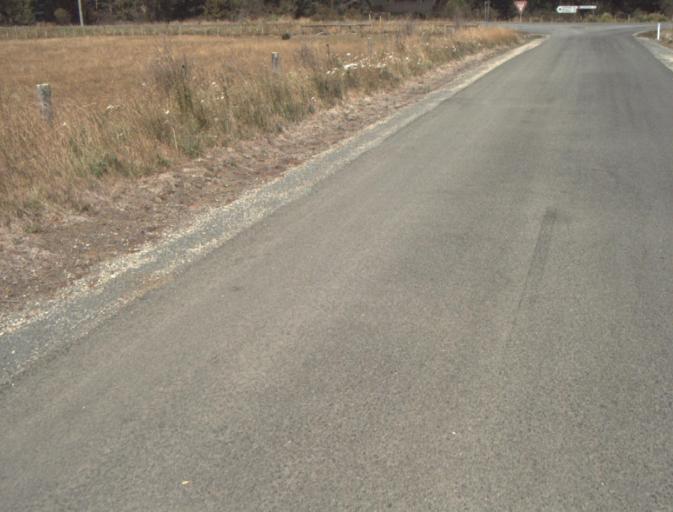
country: AU
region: Tasmania
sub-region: Dorset
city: Scottsdale
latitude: -41.3102
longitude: 147.3706
